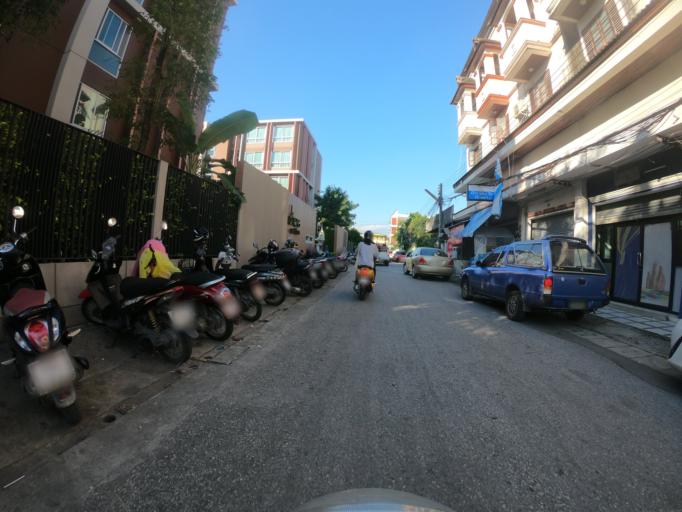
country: TH
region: Chiang Mai
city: Chiang Mai
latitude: 18.8032
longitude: 98.9823
